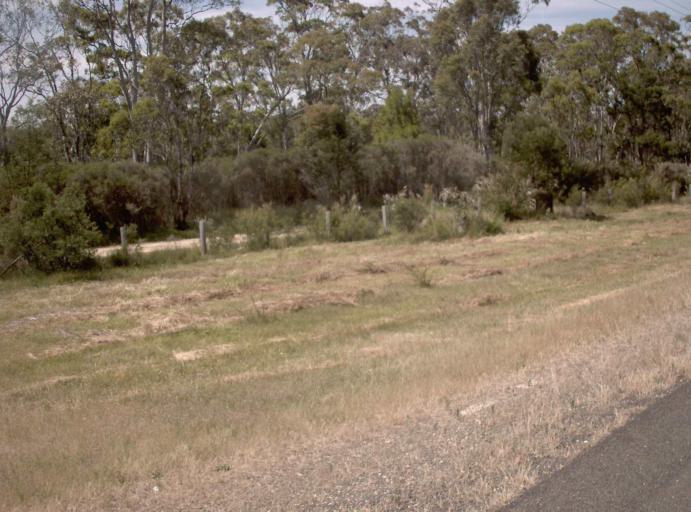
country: AU
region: Victoria
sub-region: East Gippsland
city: Bairnsdale
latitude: -37.9097
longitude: 147.3161
